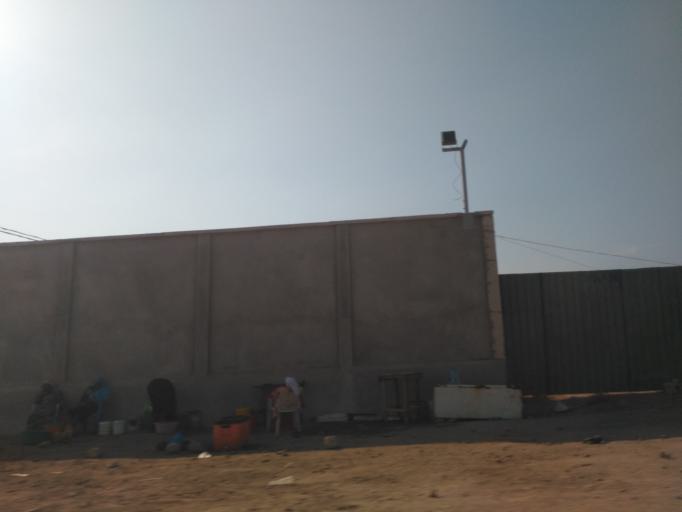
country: TZ
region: Dar es Salaam
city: Dar es Salaam
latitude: -6.8464
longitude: 39.3168
